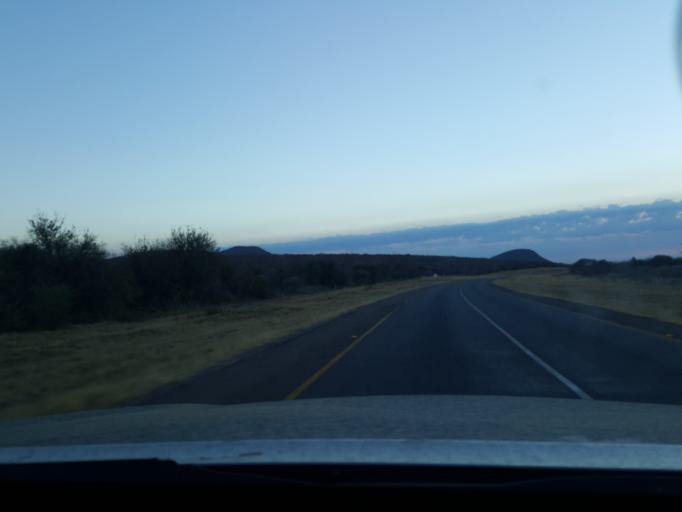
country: BW
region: South East
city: Otse
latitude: -25.0794
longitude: 25.7213
